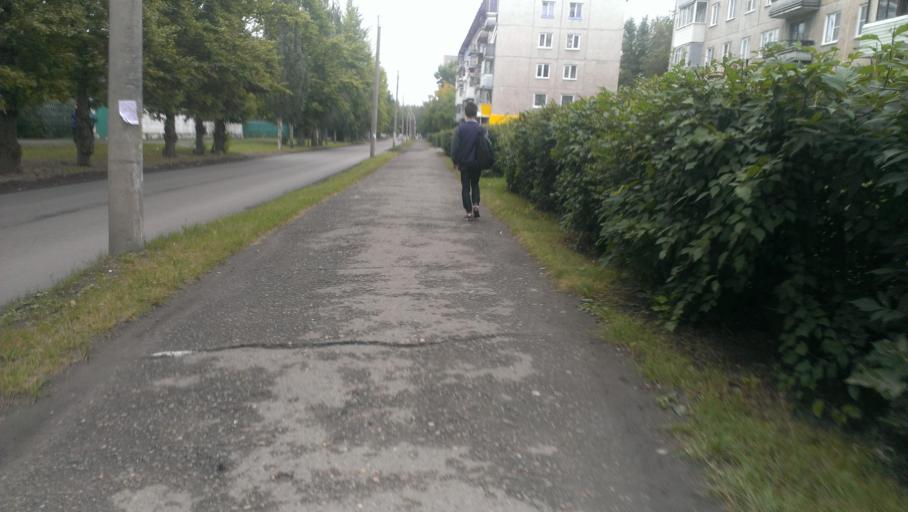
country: RU
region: Altai Krai
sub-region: Gorod Barnaulskiy
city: Barnaul
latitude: 53.3691
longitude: 83.6897
